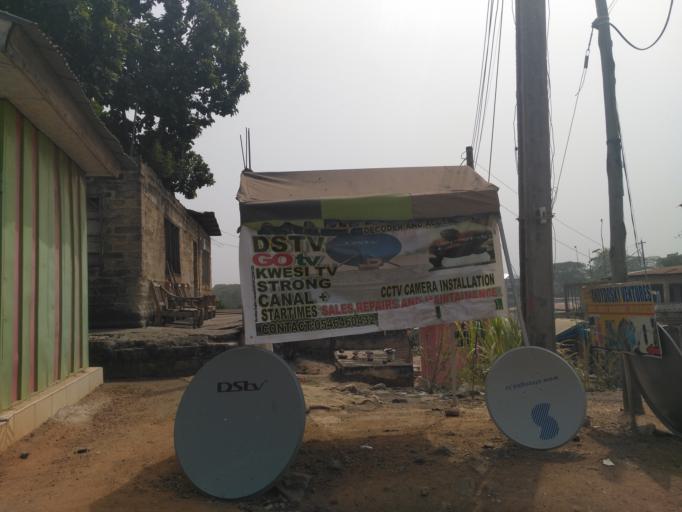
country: GH
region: Ashanti
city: Kumasi
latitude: 6.6820
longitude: -1.6002
